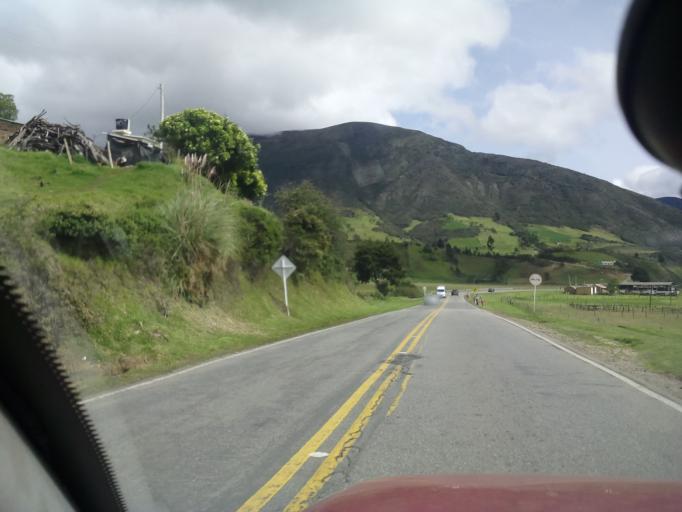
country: CO
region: Boyaca
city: Arcabuco
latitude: 5.7019
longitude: -73.3698
